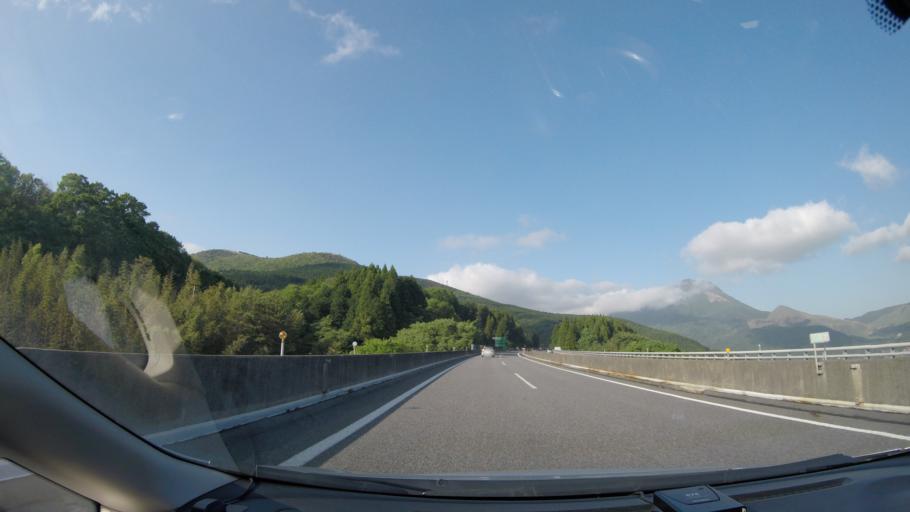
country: JP
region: Oita
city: Beppu
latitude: 33.2630
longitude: 131.3331
